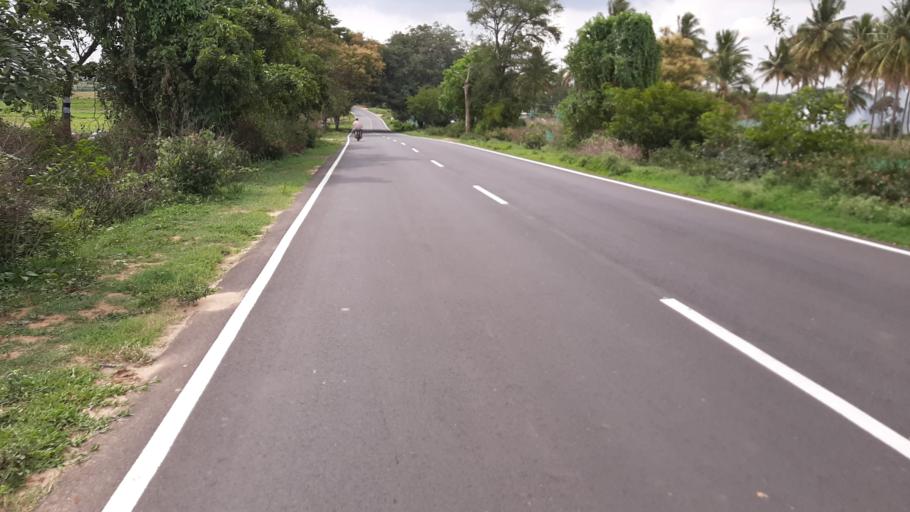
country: IN
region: Tamil Nadu
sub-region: Krishnagiri
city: Denkanikota
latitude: 12.5355
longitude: 77.7743
